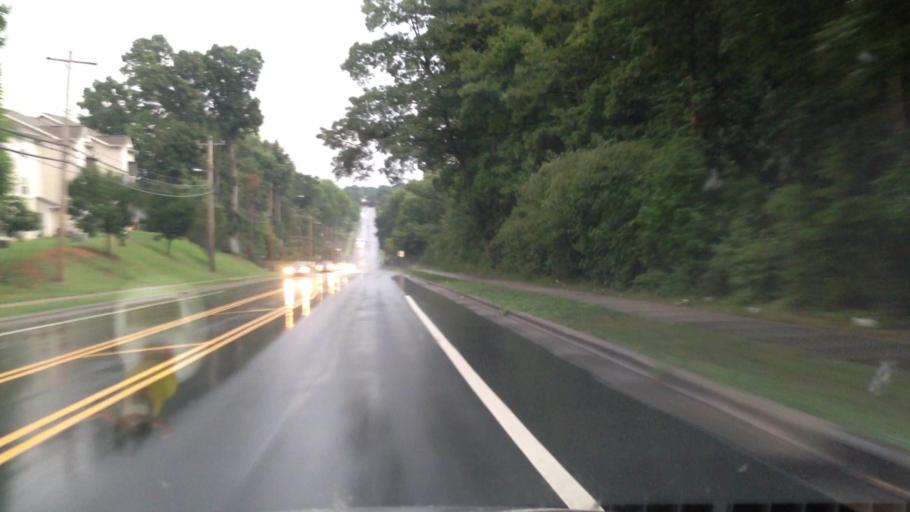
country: US
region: North Carolina
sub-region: Mecklenburg County
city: Pineville
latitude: 35.1359
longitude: -80.8901
